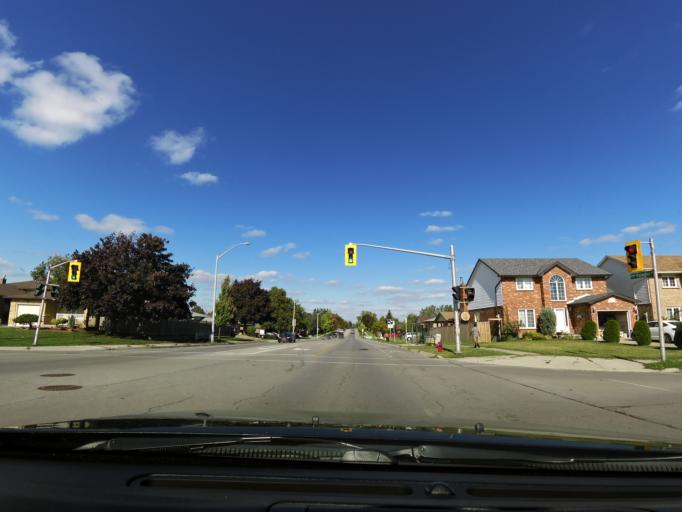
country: CA
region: Ontario
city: Ancaster
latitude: 43.2235
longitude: -79.9162
